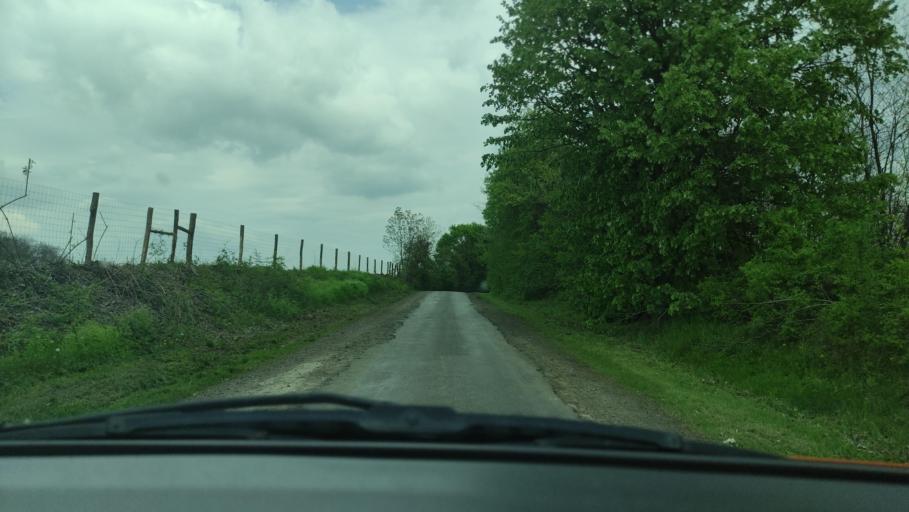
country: HU
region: Somogy
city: Taszar
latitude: 46.2965
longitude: 17.9658
